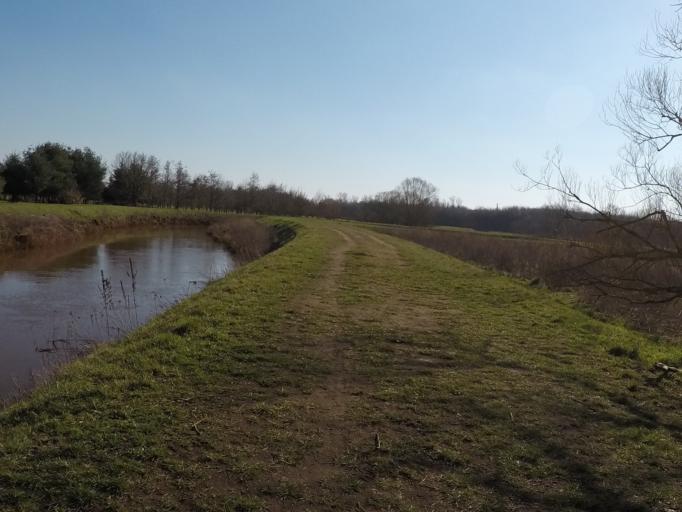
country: BE
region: Flanders
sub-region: Provincie Antwerpen
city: Herenthout
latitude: 51.1146
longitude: 4.7334
